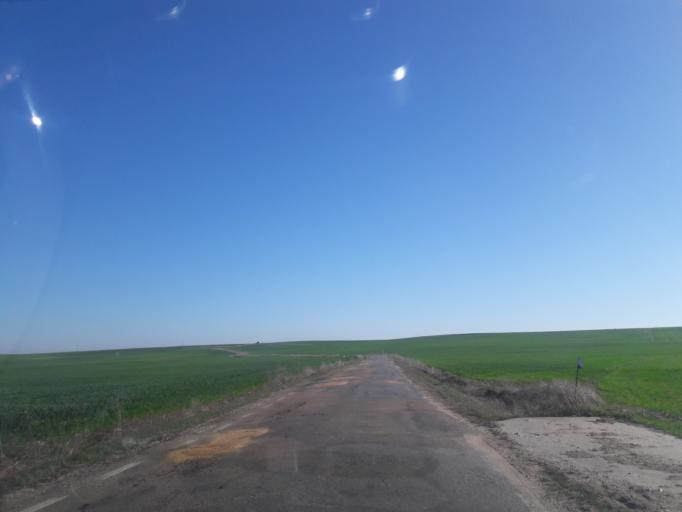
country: ES
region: Castille and Leon
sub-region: Provincia de Salamanca
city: Tordillos
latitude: 40.8701
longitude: -5.3325
